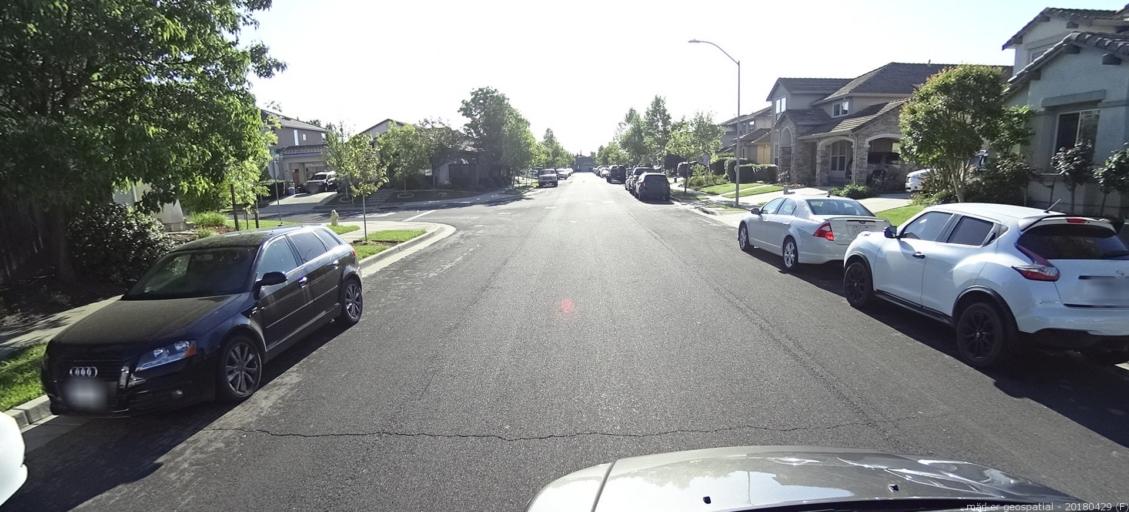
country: US
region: California
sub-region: Yolo County
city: West Sacramento
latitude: 38.5356
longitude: -121.5748
